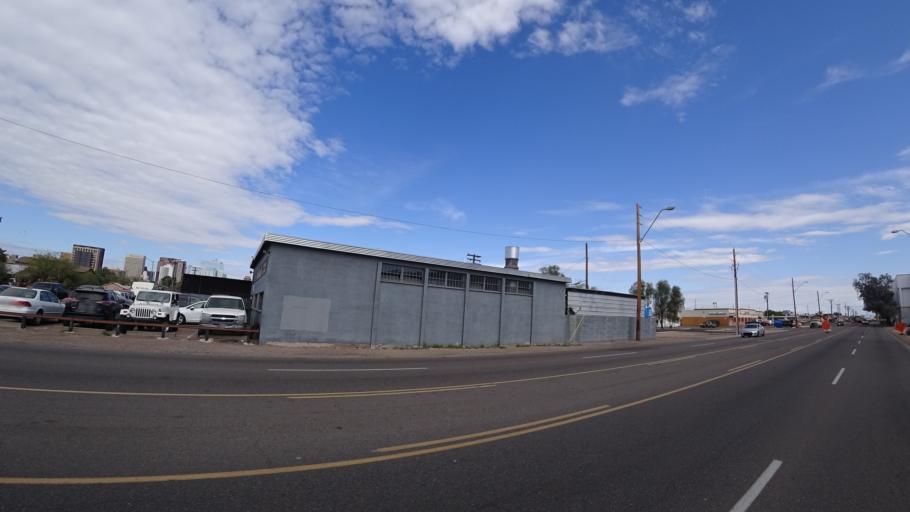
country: US
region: Arizona
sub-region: Maricopa County
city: Phoenix
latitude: 33.4368
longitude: -112.0724
